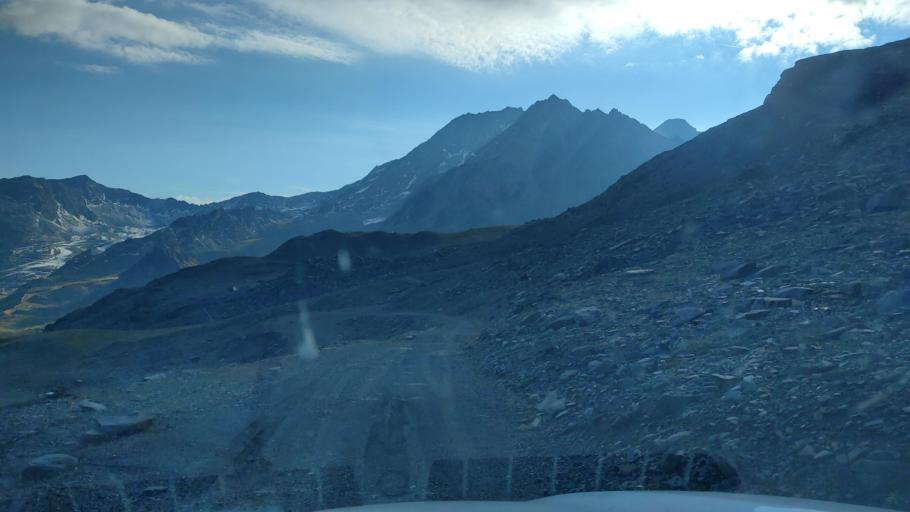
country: FR
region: Rhone-Alpes
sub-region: Departement de la Savoie
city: Val Thorens
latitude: 45.2713
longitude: 6.5763
